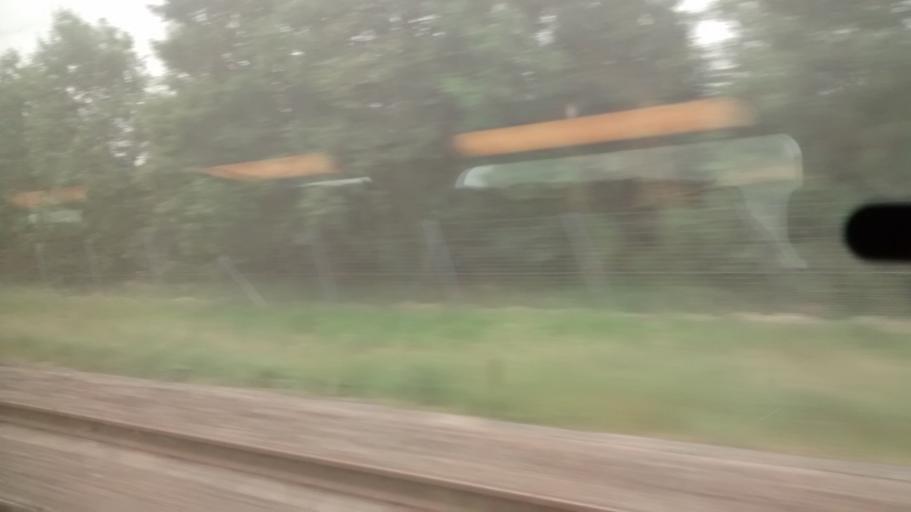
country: FR
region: Ile-de-France
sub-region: Departement de Seine-et-Marne
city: Le Chatelet-en-Brie
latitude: 48.5256
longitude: 2.8142
